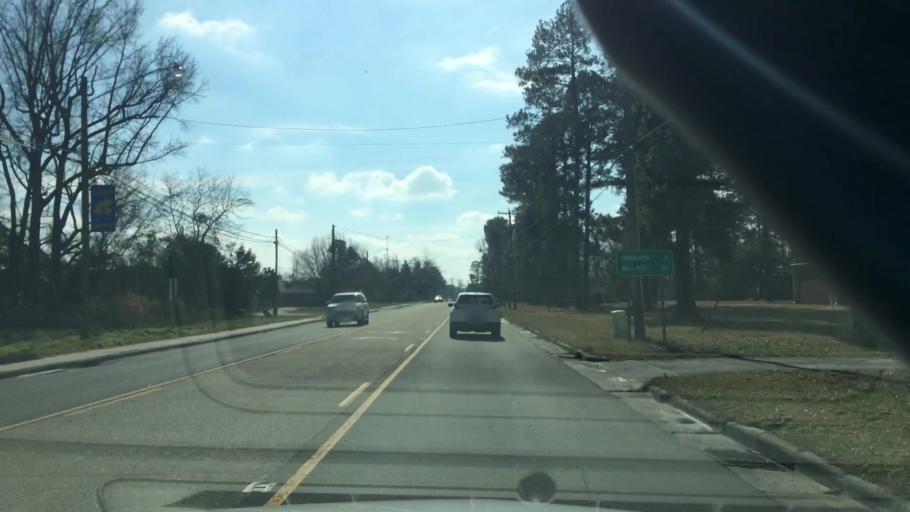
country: US
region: North Carolina
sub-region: Duplin County
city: Beulaville
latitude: 34.9206
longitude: -77.7745
